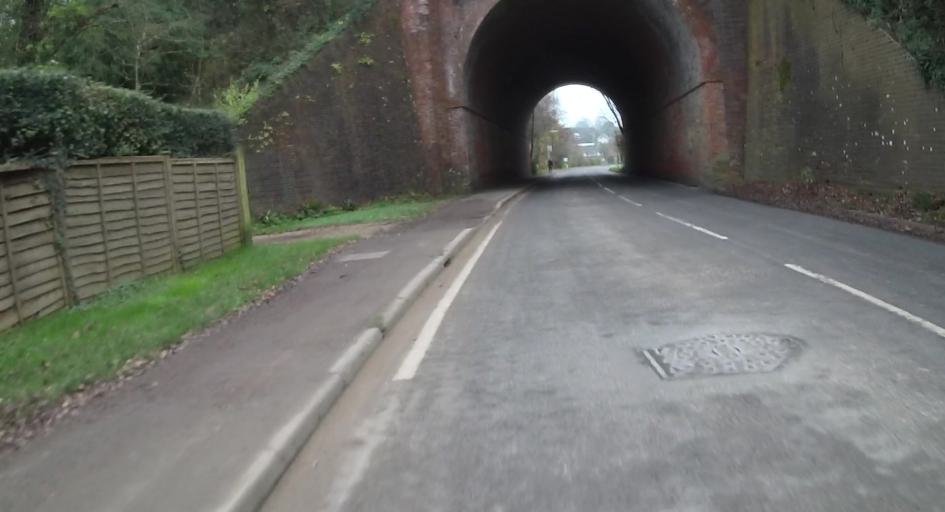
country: GB
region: England
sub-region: Hampshire
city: Kings Worthy
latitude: 51.0986
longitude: -1.3026
